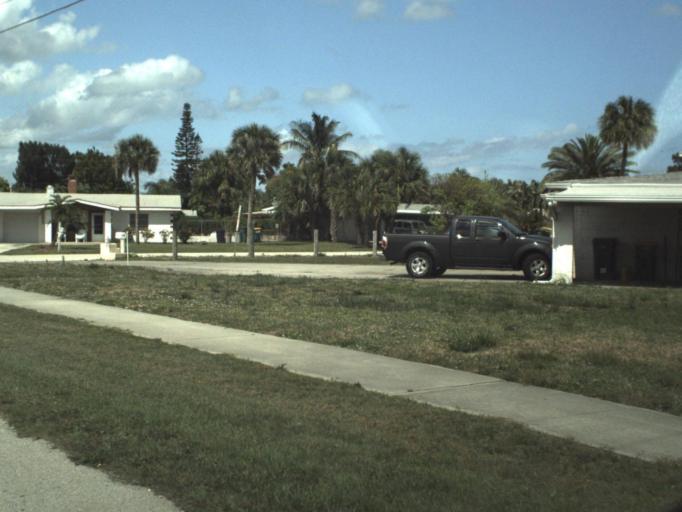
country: US
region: Florida
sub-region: Brevard County
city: Cape Canaveral
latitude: 28.3632
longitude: -80.6072
